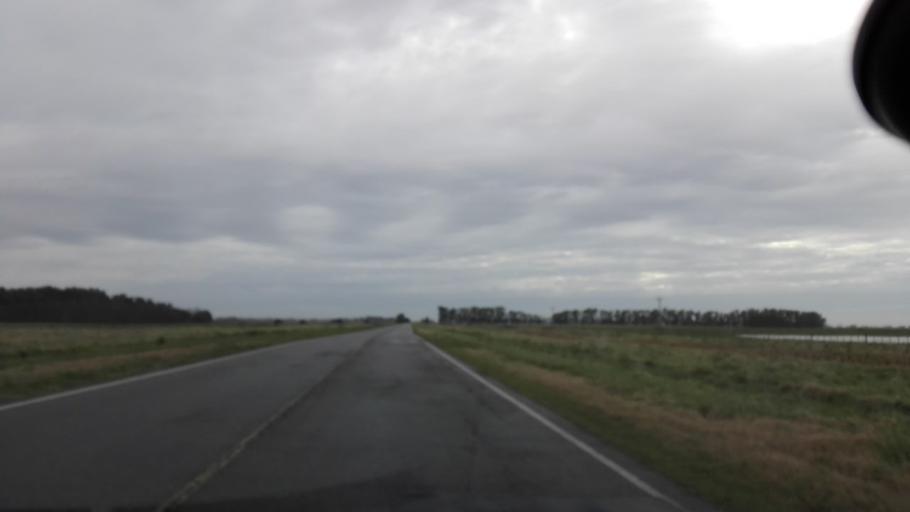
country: AR
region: Buenos Aires
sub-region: Partido de Rauch
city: Rauch
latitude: -36.6382
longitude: -59.0658
